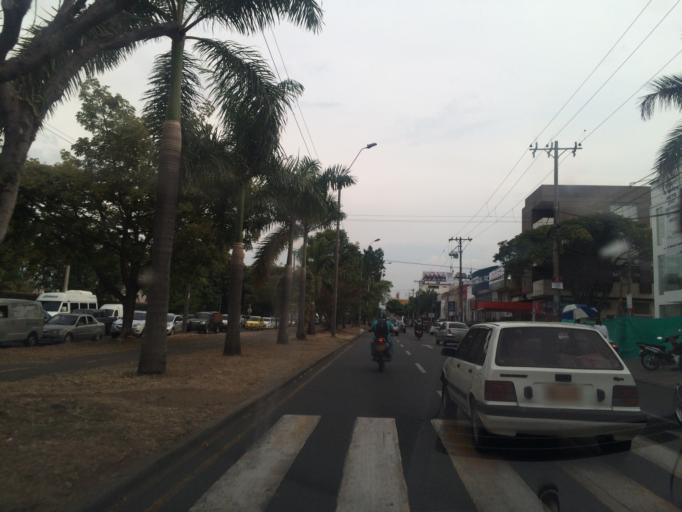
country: CO
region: Valle del Cauca
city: Cali
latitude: 3.3918
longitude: -76.5385
